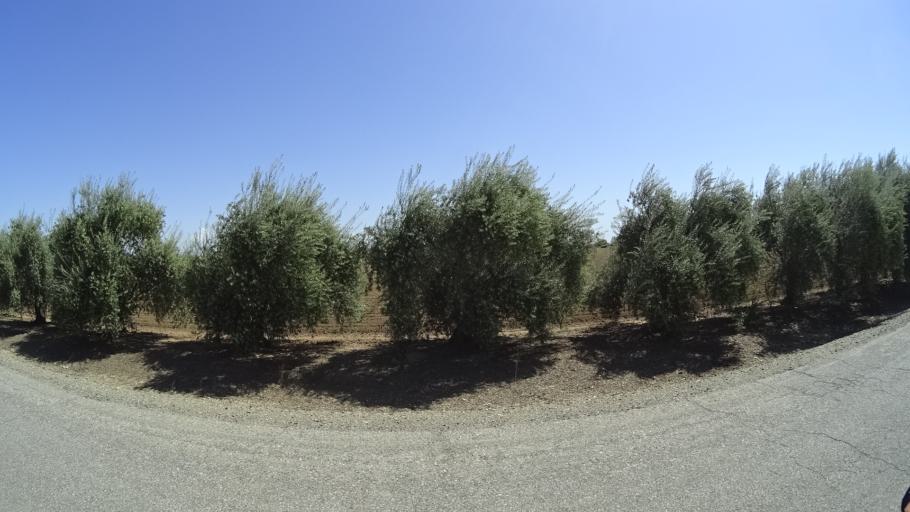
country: US
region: California
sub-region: Glenn County
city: Orland
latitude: 39.7793
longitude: -122.1690
